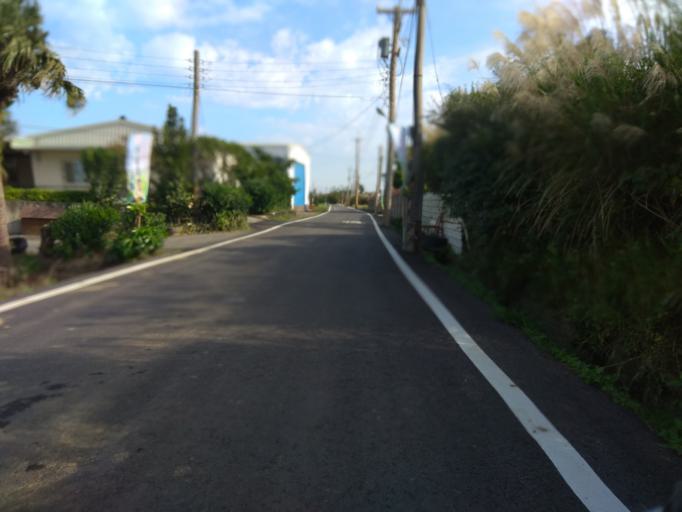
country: TW
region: Taiwan
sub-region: Hsinchu
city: Zhubei
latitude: 24.9983
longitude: 121.0433
